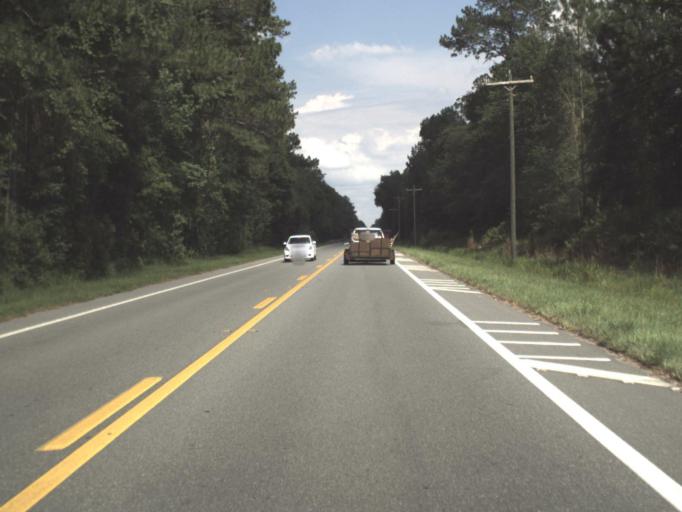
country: US
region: Florida
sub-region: Putnam County
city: Palatka
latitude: 29.6900
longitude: -81.7460
